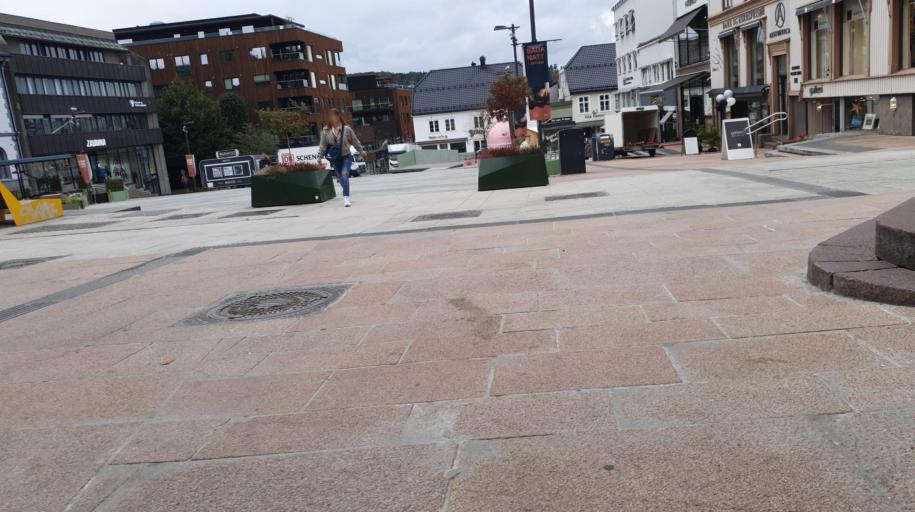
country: NO
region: Vestfold
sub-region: Tonsberg
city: Tonsberg
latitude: 59.2681
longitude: 10.4084
